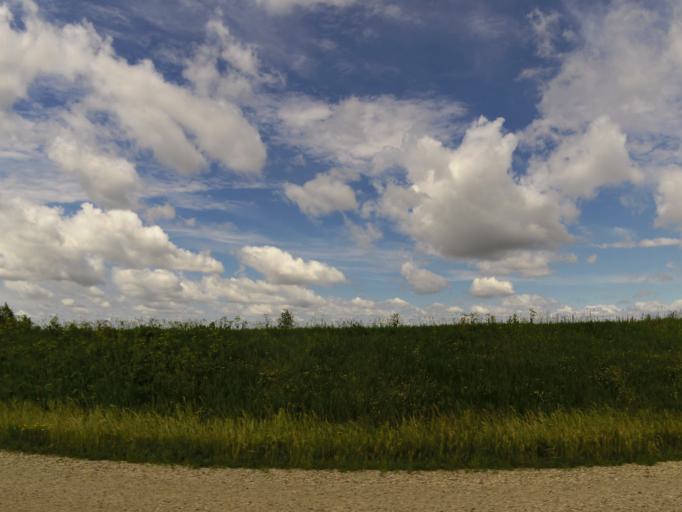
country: US
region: Iowa
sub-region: Chickasaw County
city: New Hampton
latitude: 43.1933
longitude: -92.2982
